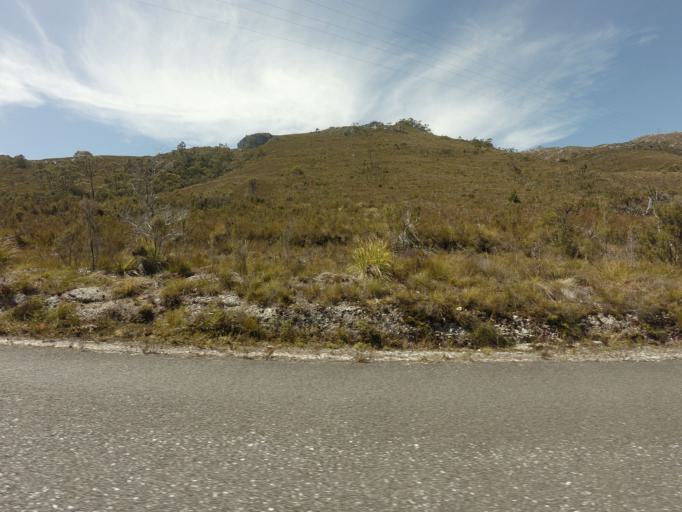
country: AU
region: Tasmania
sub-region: West Coast
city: Queenstown
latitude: -42.7700
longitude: 146.0568
